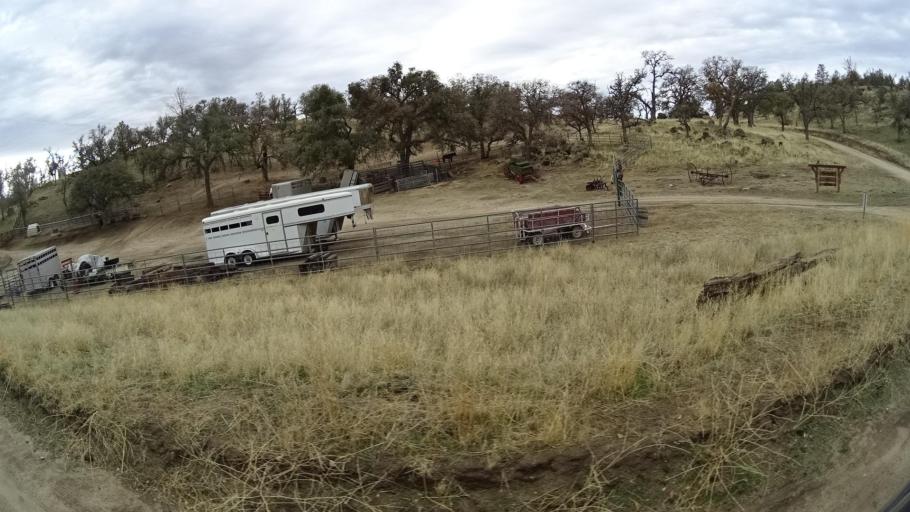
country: US
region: California
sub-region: Kern County
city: Stallion Springs
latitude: 35.1106
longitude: -118.6780
